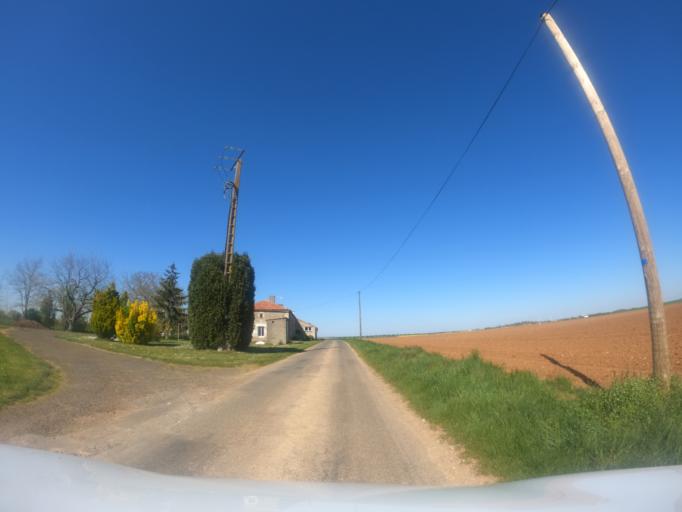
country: FR
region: Pays de la Loire
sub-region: Departement de la Vendee
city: Fontenay-le-Comte
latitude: 46.4214
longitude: -0.7966
